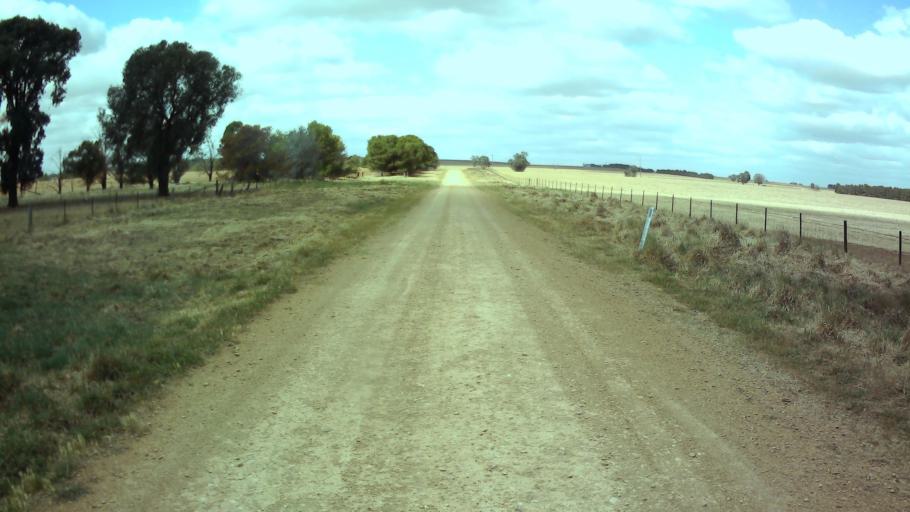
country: AU
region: New South Wales
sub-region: Weddin
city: Grenfell
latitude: -34.0625
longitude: 148.3298
